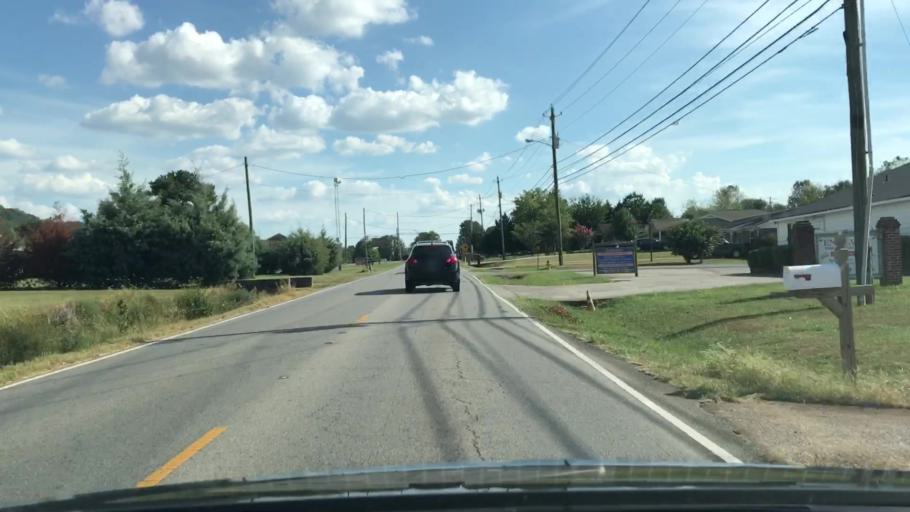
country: US
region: Alabama
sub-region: Madison County
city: Harvest
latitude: 34.8326
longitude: -86.7492
